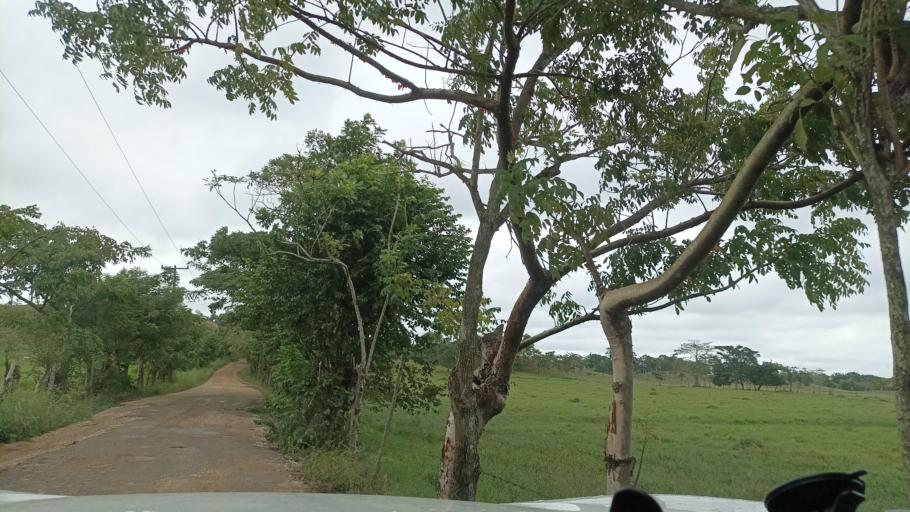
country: MX
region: Veracruz
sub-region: Moloacan
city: Cuichapa
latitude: 17.7937
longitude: -94.3813
